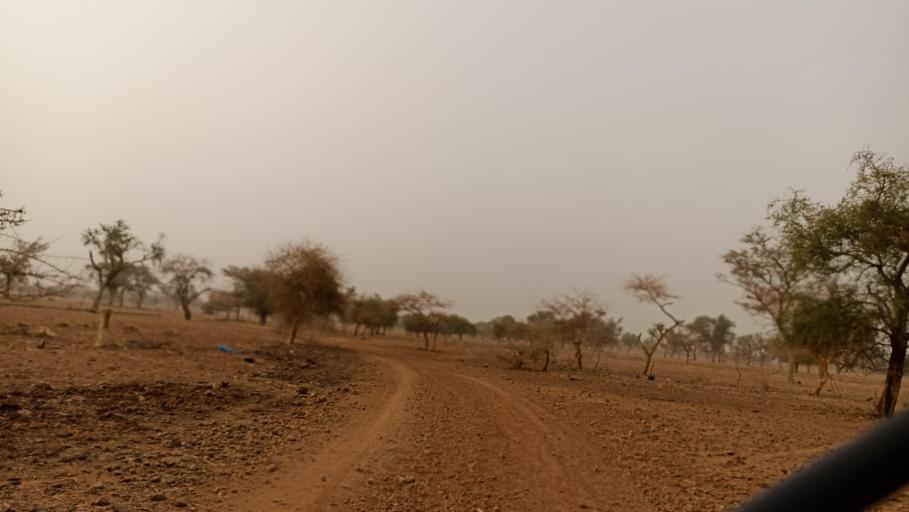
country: BF
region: Nord
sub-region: Province du Zondoma
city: Gourcy
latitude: 13.2381
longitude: -2.5849
